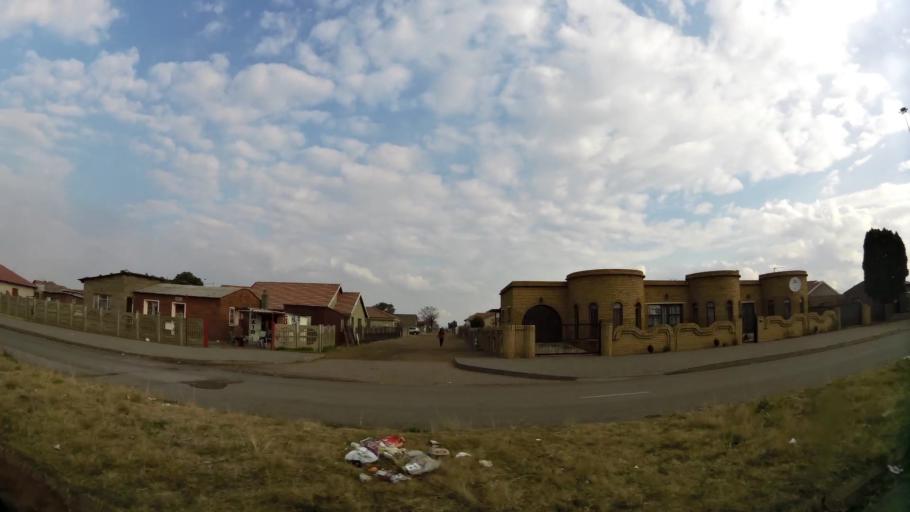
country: ZA
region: Gauteng
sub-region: Sedibeng District Municipality
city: Vanderbijlpark
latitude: -26.6887
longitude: 27.8720
